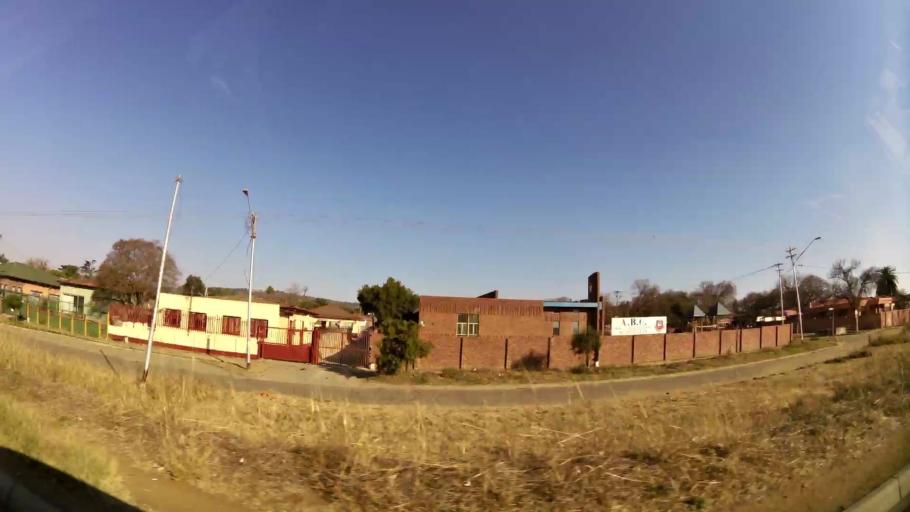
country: ZA
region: Gauteng
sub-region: City of Tshwane Metropolitan Municipality
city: Pretoria
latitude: -25.7440
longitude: 28.1523
